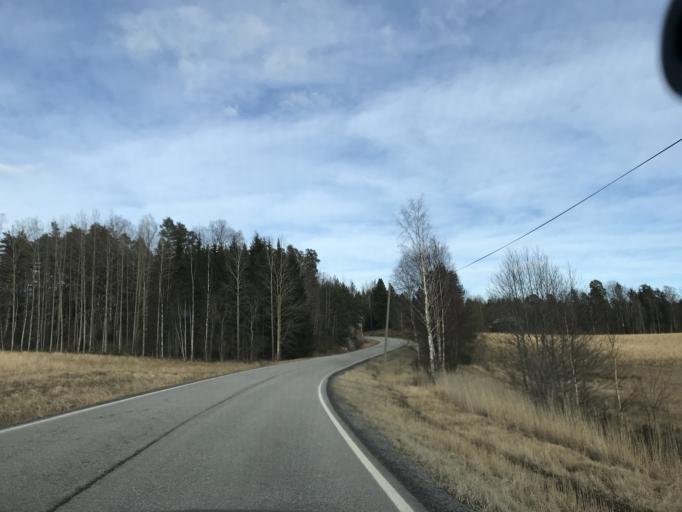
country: FI
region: Uusimaa
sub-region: Raaseporin
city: Pohja
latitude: 60.0903
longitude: 23.4543
